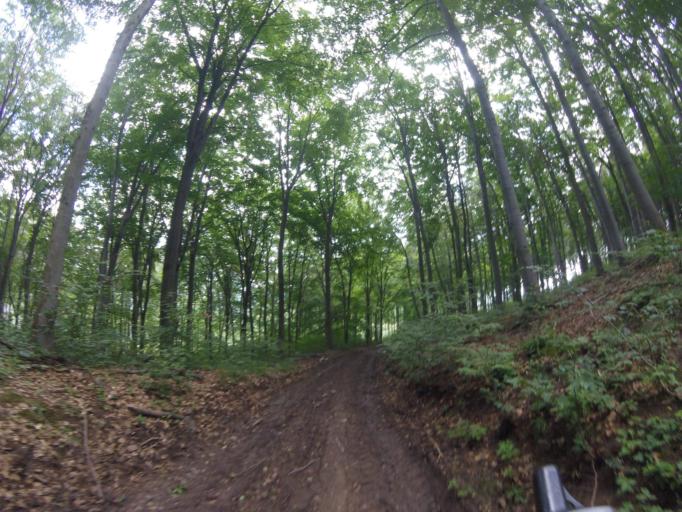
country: SK
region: Nitriansky
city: Sahy
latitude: 47.9562
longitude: 18.8859
